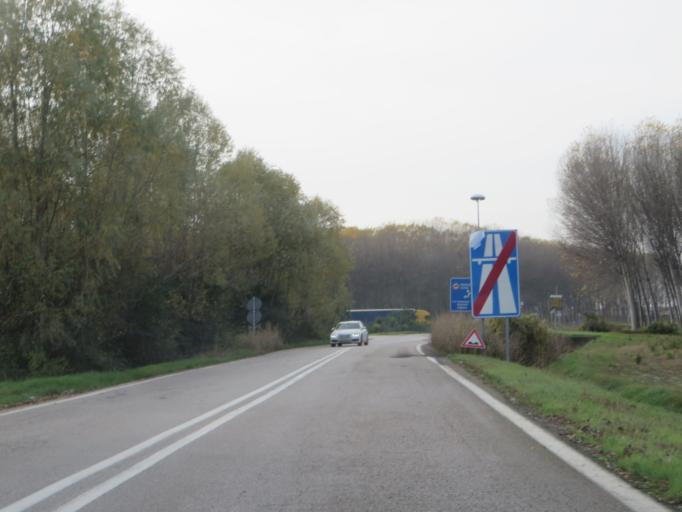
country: IT
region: Veneto
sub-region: Provincia di Verona
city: San Pietro di Morubio
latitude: 45.2293
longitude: 11.2348
